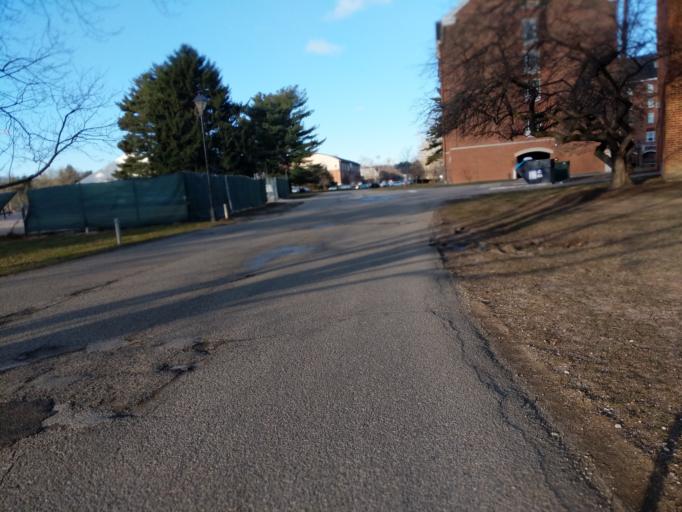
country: US
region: Ohio
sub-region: Athens County
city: Athens
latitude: 39.3218
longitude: -82.0946
